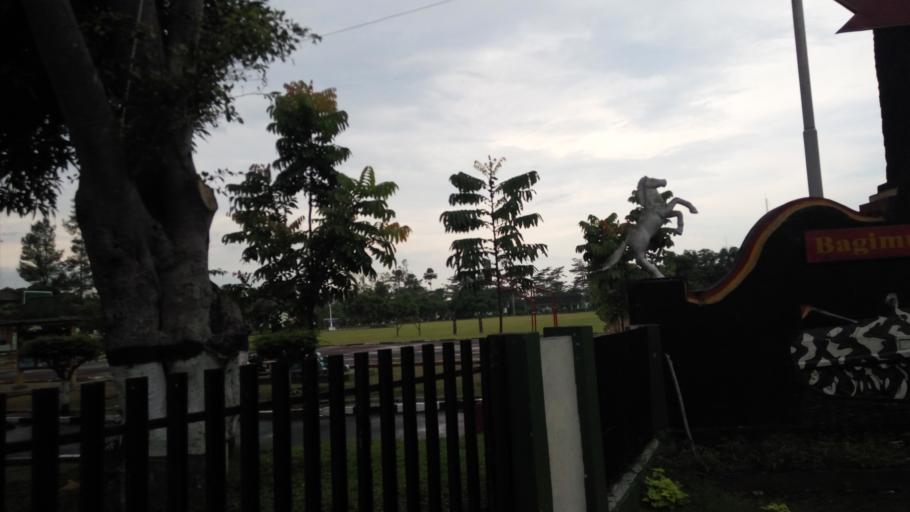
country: ID
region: Central Java
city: Ambarawa
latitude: -7.2681
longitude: 110.4033
